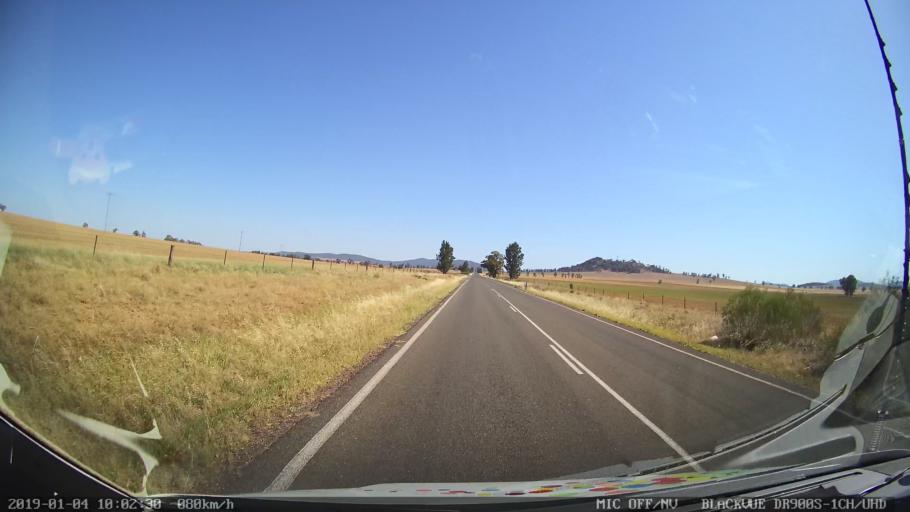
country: AU
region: New South Wales
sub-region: Cabonne
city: Canowindra
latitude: -33.4756
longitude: 148.3654
